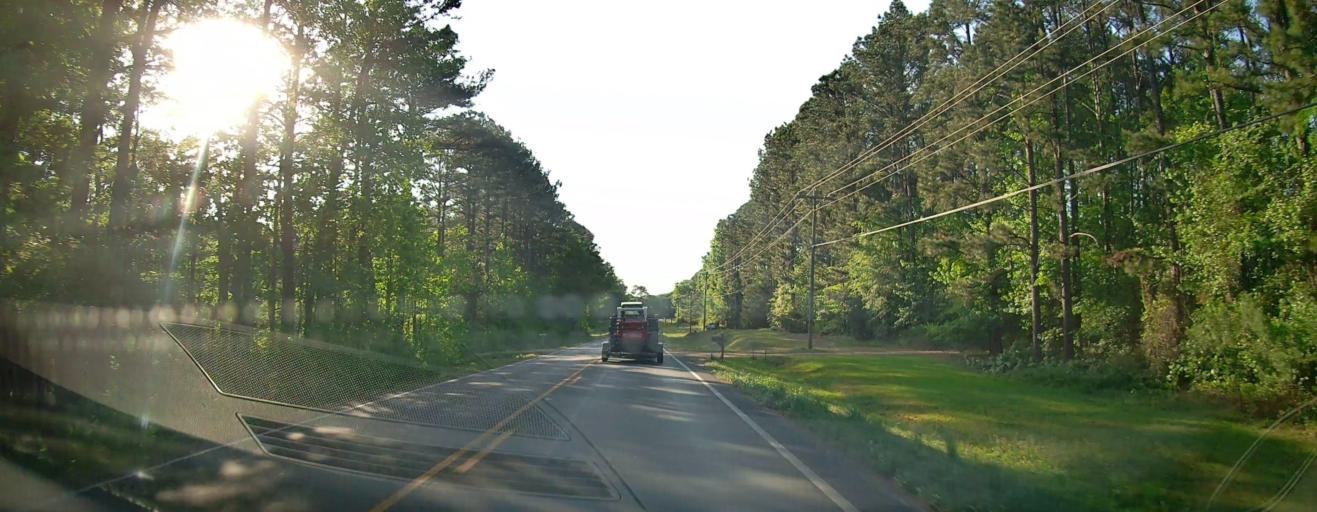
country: US
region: Georgia
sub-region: Putnam County
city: Eatonton
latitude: 33.3100
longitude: -83.4874
